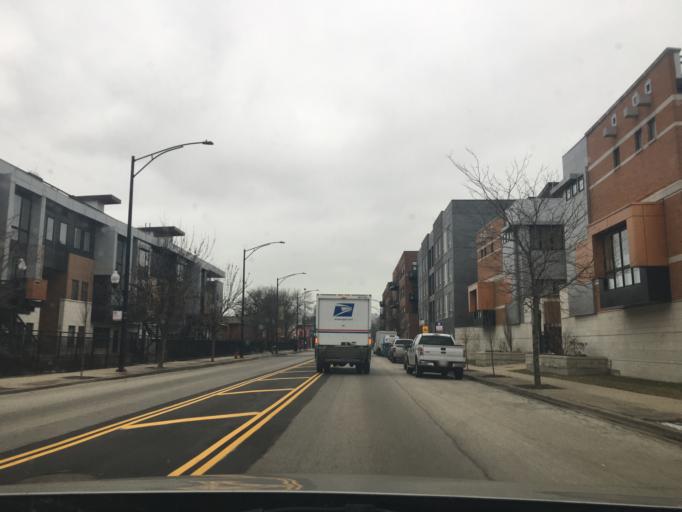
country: US
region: Illinois
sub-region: Cook County
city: Chicago
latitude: 41.8812
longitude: -87.6824
